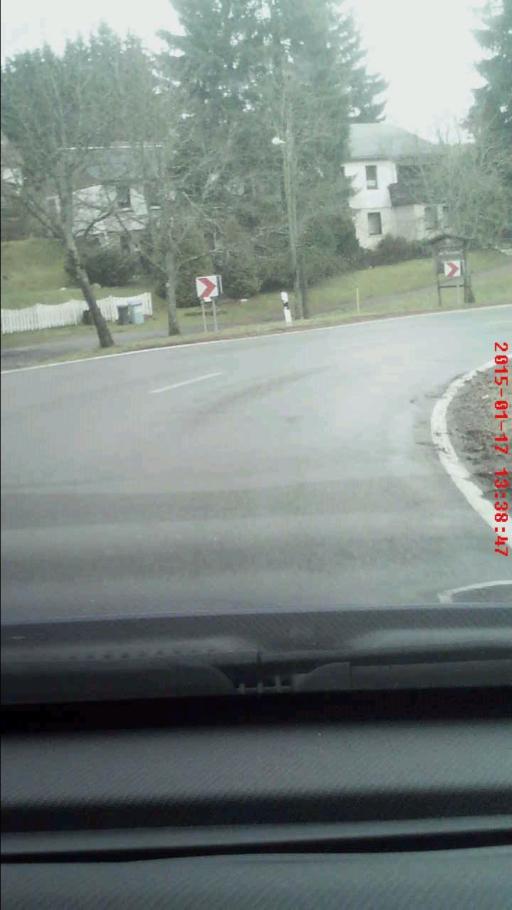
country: DE
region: Thuringia
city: Grossbreitenbach
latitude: 50.5790
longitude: 11.0094
